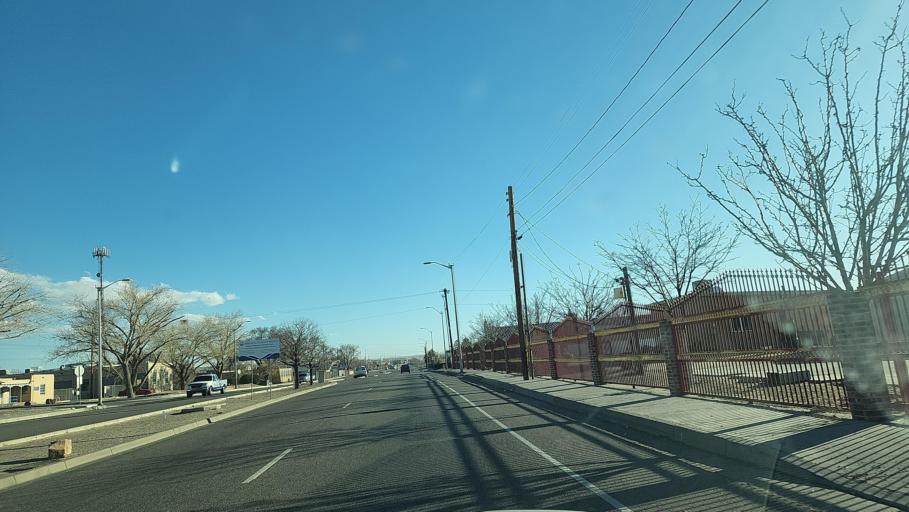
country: US
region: New Mexico
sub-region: Bernalillo County
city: Albuquerque
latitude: 35.0591
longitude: -106.6453
